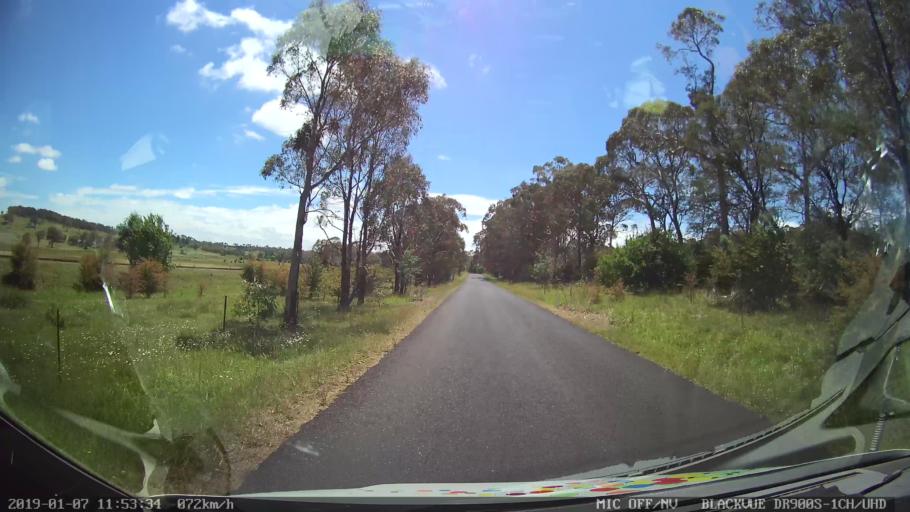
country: AU
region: New South Wales
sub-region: Guyra
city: Guyra
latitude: -30.3034
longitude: 151.6586
